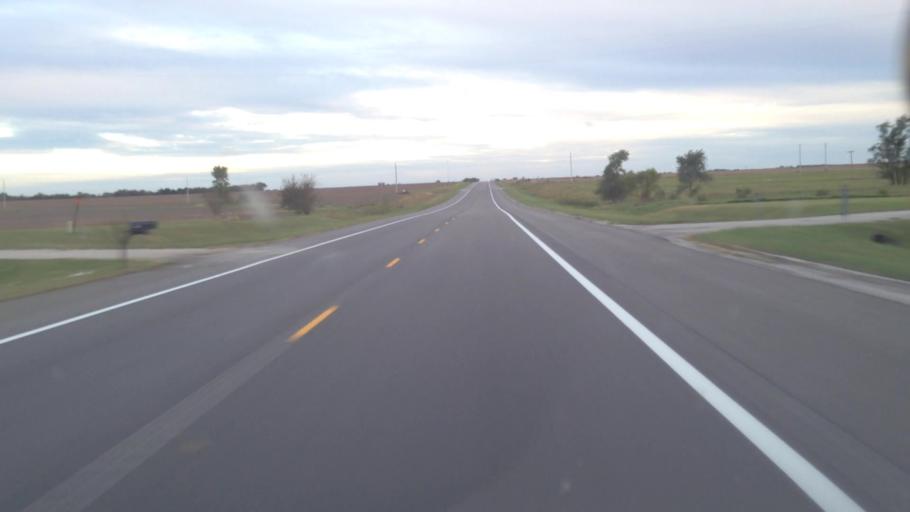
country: US
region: Kansas
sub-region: Franklin County
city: Ottawa
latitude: 38.4516
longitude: -95.2488
